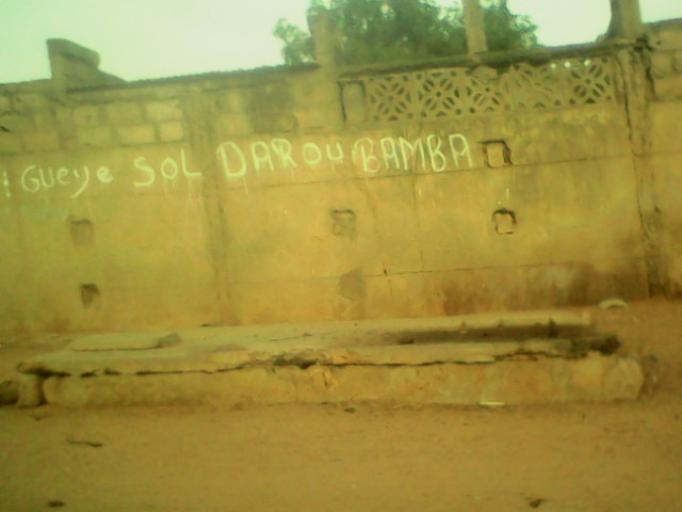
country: SN
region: Diourbel
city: Touba
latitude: 14.8653
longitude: -15.8832
